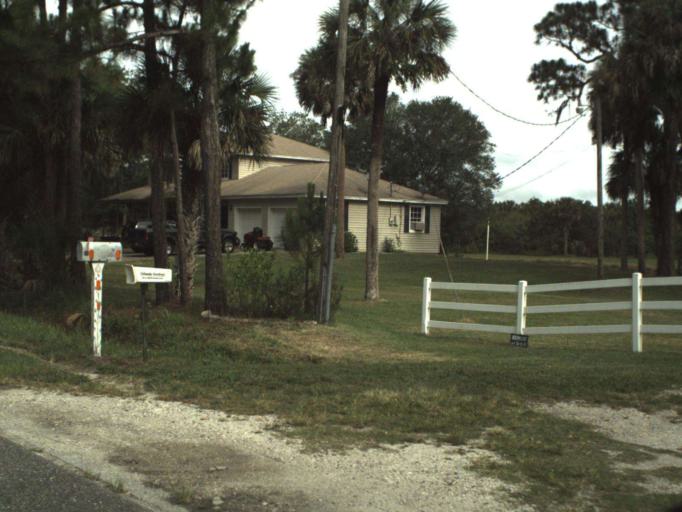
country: US
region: Florida
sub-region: Seminole County
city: Geneva
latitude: 28.7162
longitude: -81.0525
